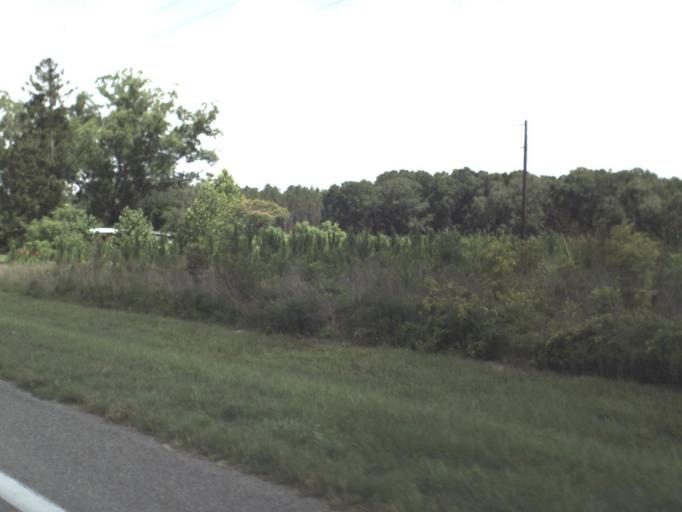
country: US
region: Florida
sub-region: Lafayette County
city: Mayo
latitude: 29.9507
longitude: -82.9529
